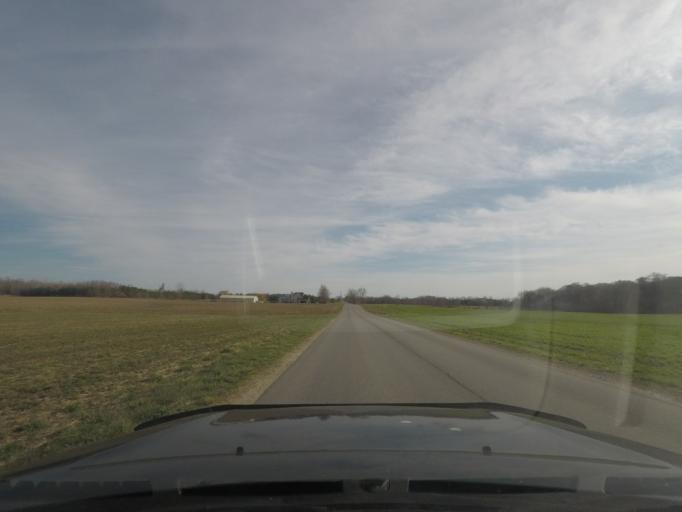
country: US
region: Indiana
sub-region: Elkhart County
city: Dunlap
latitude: 41.5608
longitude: -85.9249
